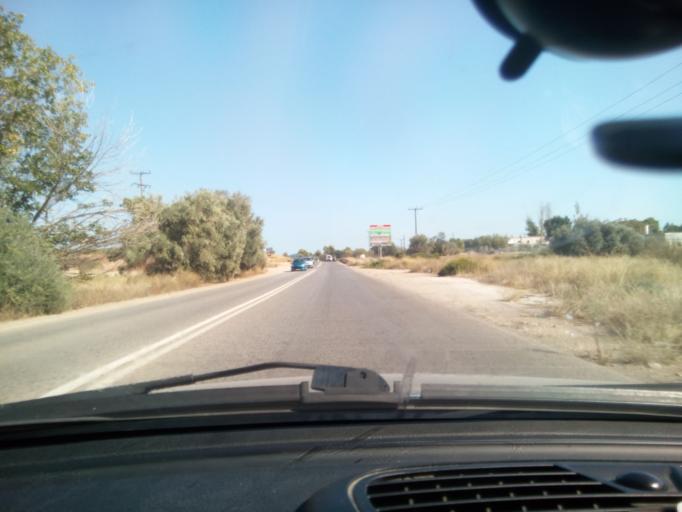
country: GR
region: Central Greece
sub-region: Nomos Evvoias
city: Filla
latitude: 38.4157
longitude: 23.7102
